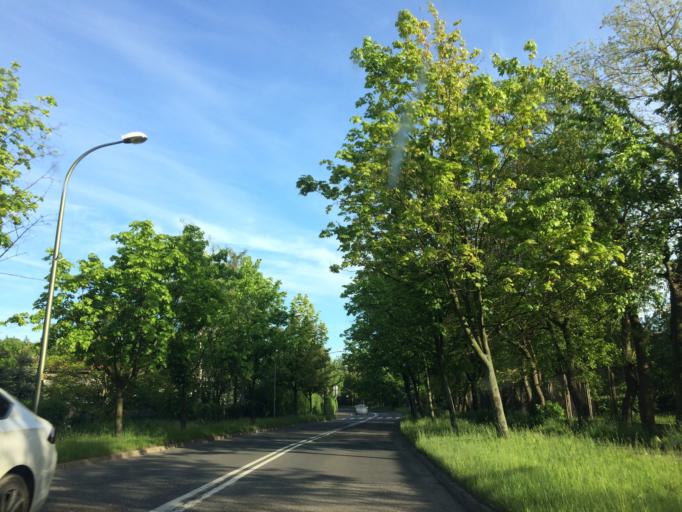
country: PL
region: Lower Silesian Voivodeship
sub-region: Powiat swidnicki
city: Swidnica
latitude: 50.8429
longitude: 16.4708
